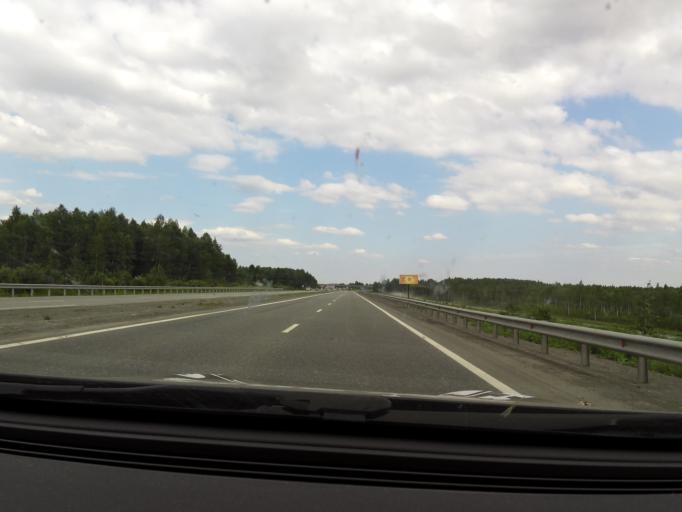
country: RU
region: Sverdlovsk
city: Talitsa
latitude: 56.8379
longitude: 60.1375
